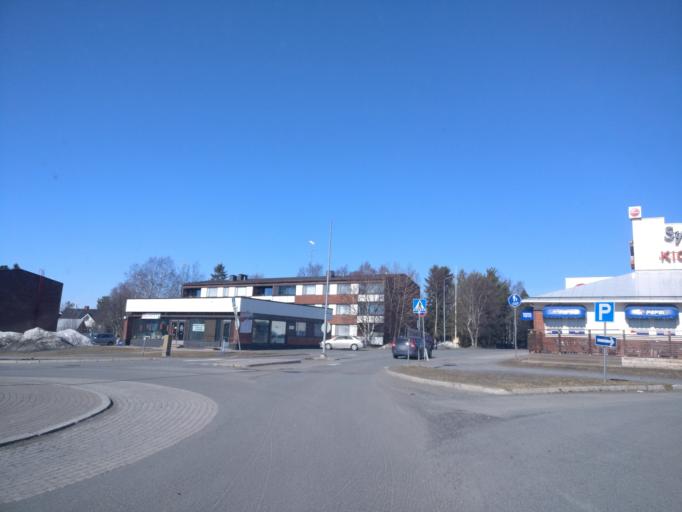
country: FI
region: Lapland
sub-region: Kemi-Tornio
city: Kemi
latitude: 65.7296
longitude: 24.6023
